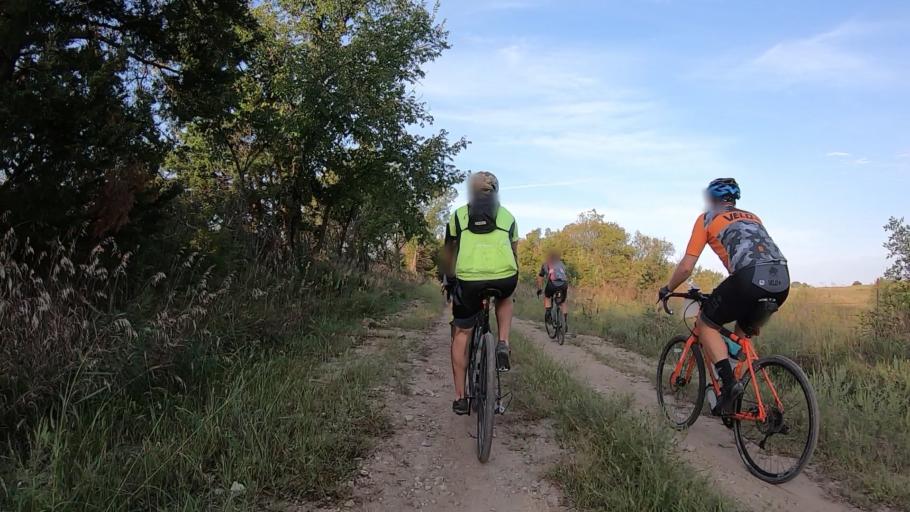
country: US
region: Kansas
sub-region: Marshall County
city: Marysville
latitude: 39.7657
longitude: -96.7052
